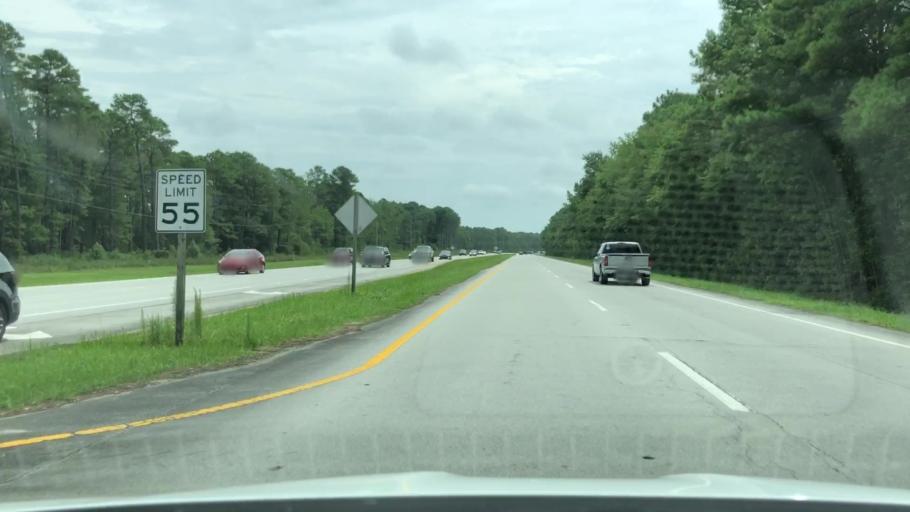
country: US
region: North Carolina
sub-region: Craven County
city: Havelock
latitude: 34.8542
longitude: -76.8933
